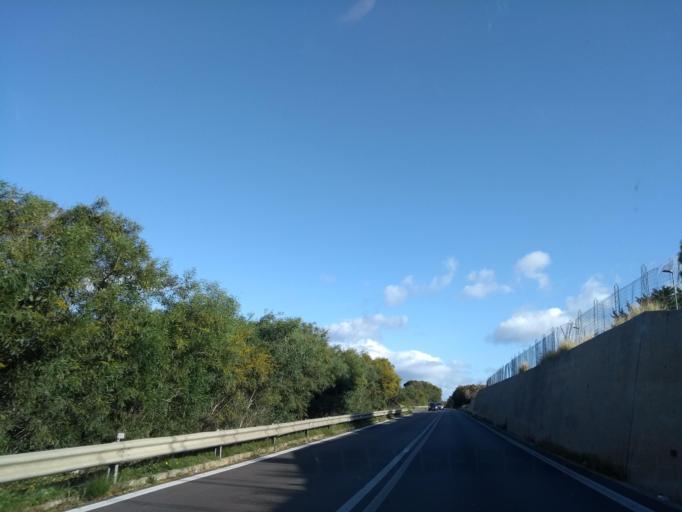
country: IT
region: Sicily
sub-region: Trapani
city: Alcamo
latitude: 38.0098
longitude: 12.9615
